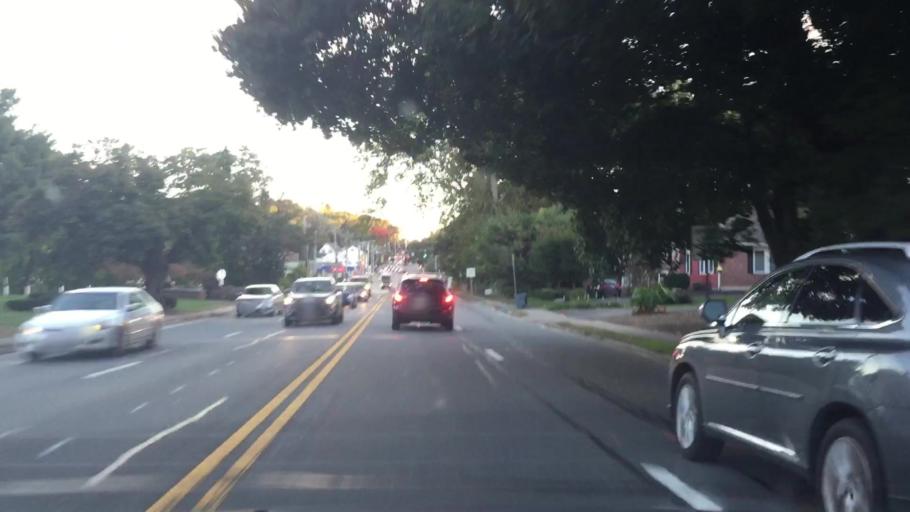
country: US
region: Massachusetts
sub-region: Essex County
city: Andover
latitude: 42.6661
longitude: -71.1468
